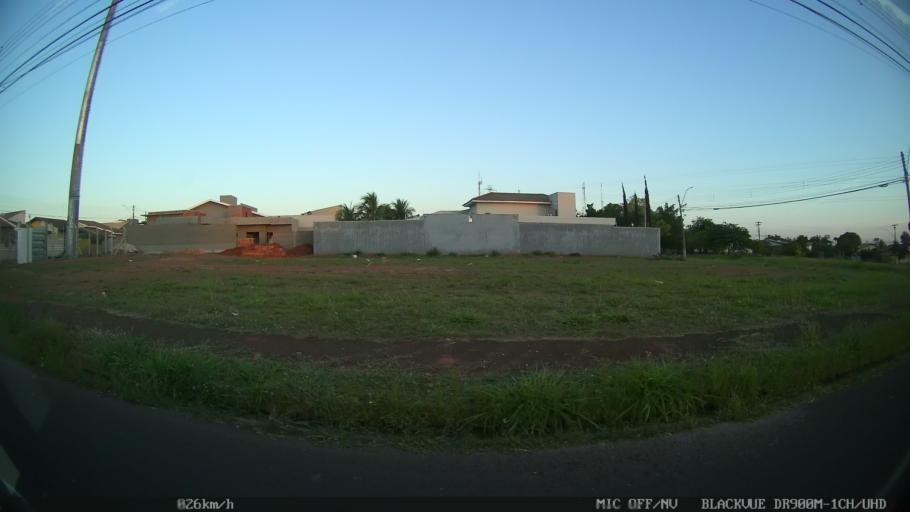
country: BR
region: Sao Paulo
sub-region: Sao Jose Do Rio Preto
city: Sao Jose do Rio Preto
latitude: -20.7975
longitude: -49.3494
